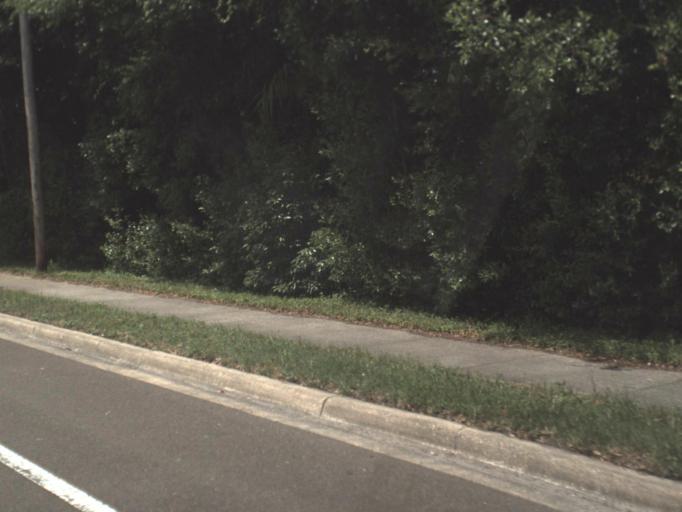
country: US
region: Florida
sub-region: Duval County
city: Jacksonville
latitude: 30.2768
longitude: -81.6505
